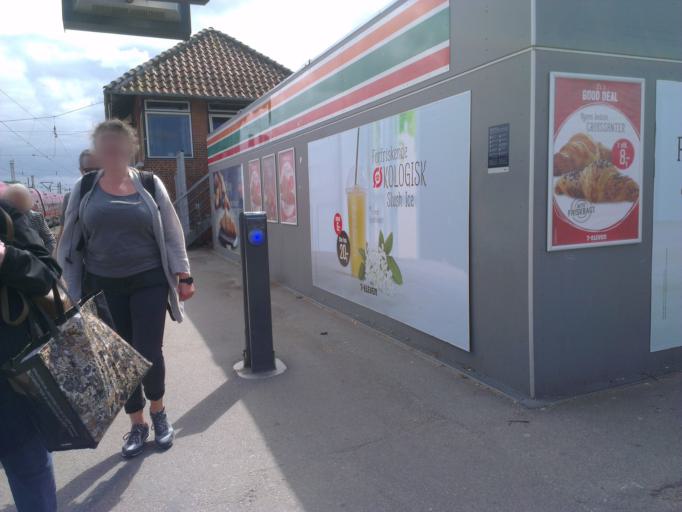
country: DK
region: Capital Region
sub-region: Hillerod Kommune
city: Hillerod
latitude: 55.9274
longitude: 12.3113
